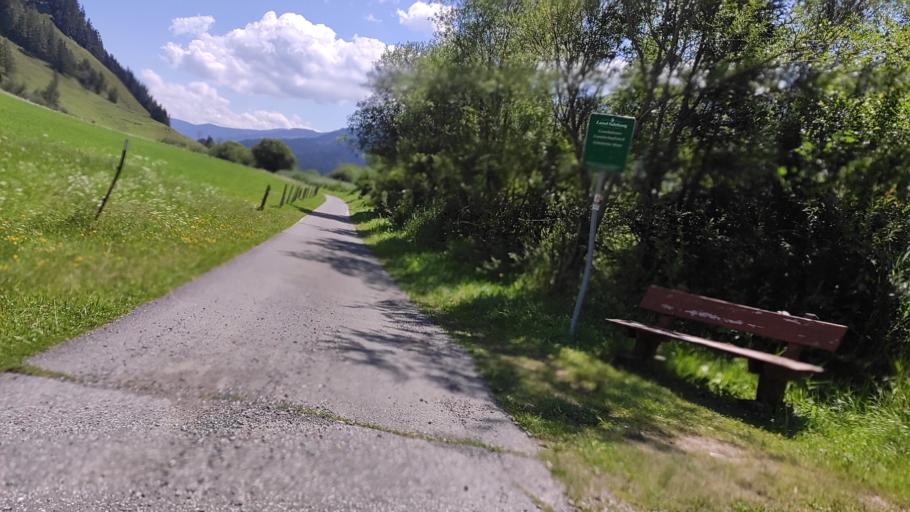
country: AT
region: Tyrol
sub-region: Politischer Bezirk Kitzbuhel
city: Hochfilzen
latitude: 47.4648
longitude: 12.6379
